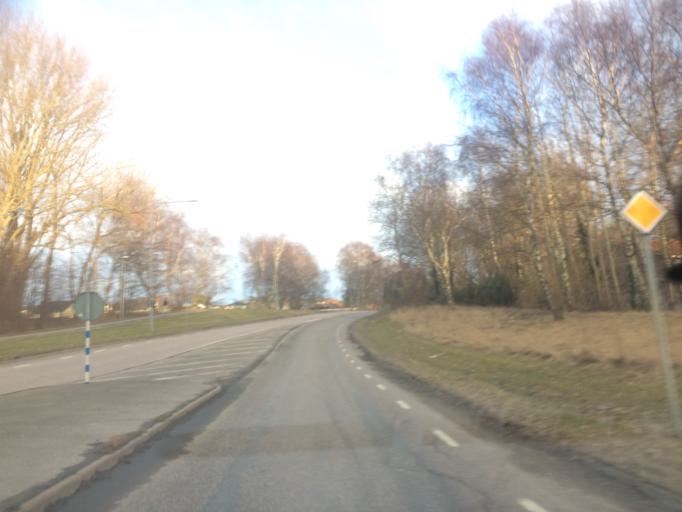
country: SE
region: Vaestra Goetaland
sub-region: Goteborg
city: Majorna
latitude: 57.6476
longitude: 11.8812
